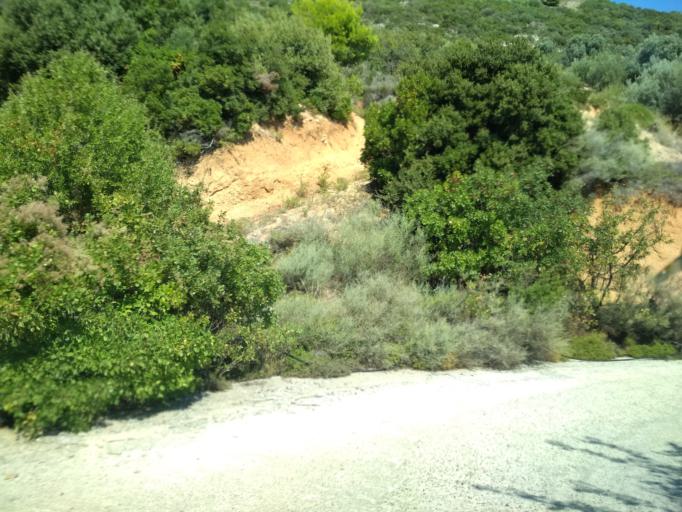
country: GR
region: Central Greece
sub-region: Nomos Evvoias
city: Oreoi
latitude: 38.8504
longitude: 23.1046
